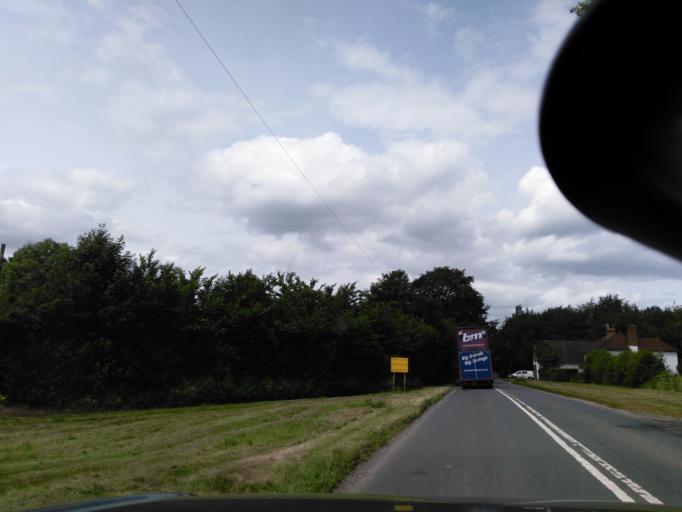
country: GB
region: England
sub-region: Wiltshire
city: Winterbourne Stoke
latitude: 51.1509
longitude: -1.8591
